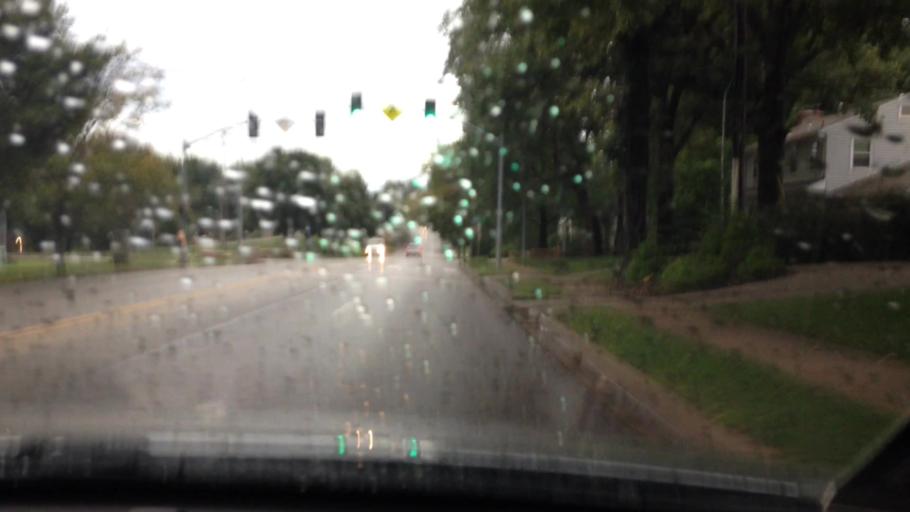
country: US
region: Kansas
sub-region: Johnson County
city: Mission Hills
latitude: 39.0042
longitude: -94.5938
